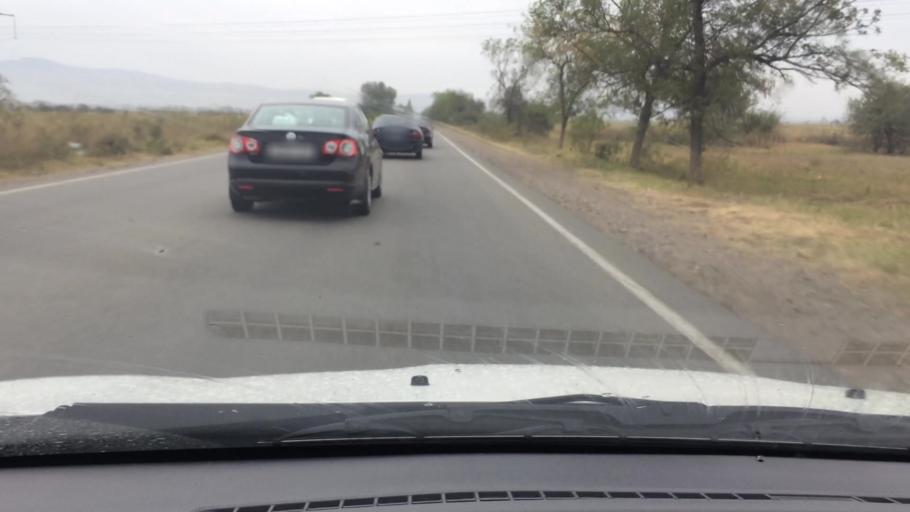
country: GE
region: Kvemo Kartli
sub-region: Marneuli
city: Marneuli
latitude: 41.5433
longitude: 44.7768
